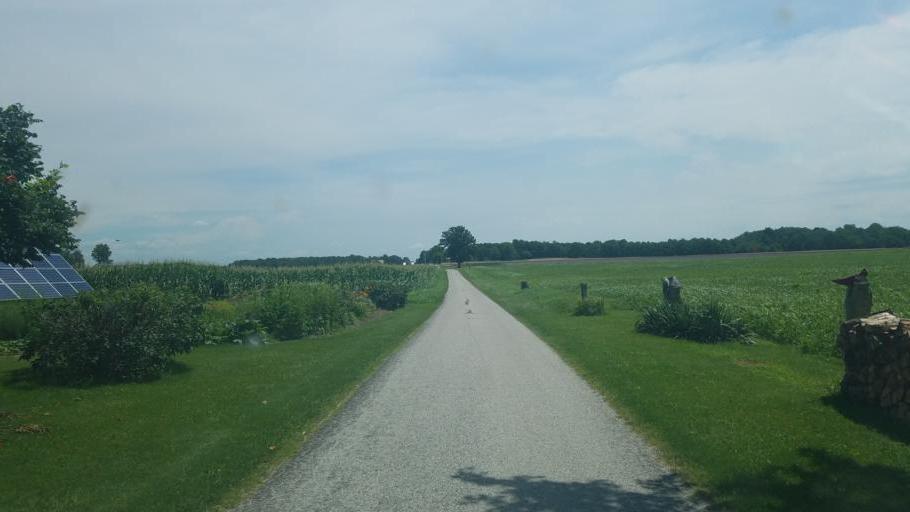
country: US
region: Ohio
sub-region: Crawford County
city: Bucyrus
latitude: 40.8739
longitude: -82.9523
